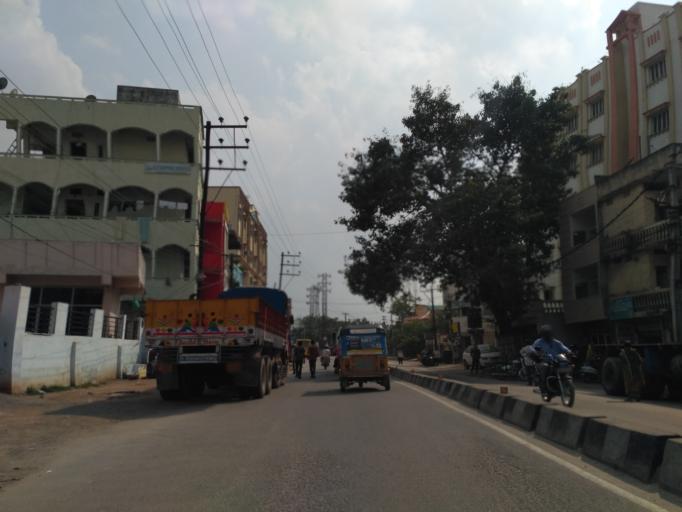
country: IN
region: Telangana
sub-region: Rangareddi
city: Kukatpalli
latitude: 17.4674
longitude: 78.4261
